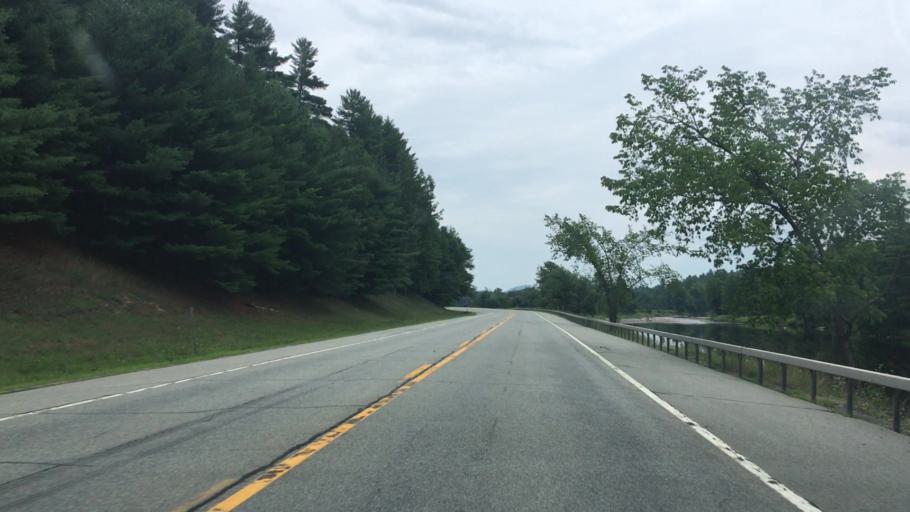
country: US
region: New York
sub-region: Essex County
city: Elizabethtown
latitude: 44.3548
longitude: -73.7522
